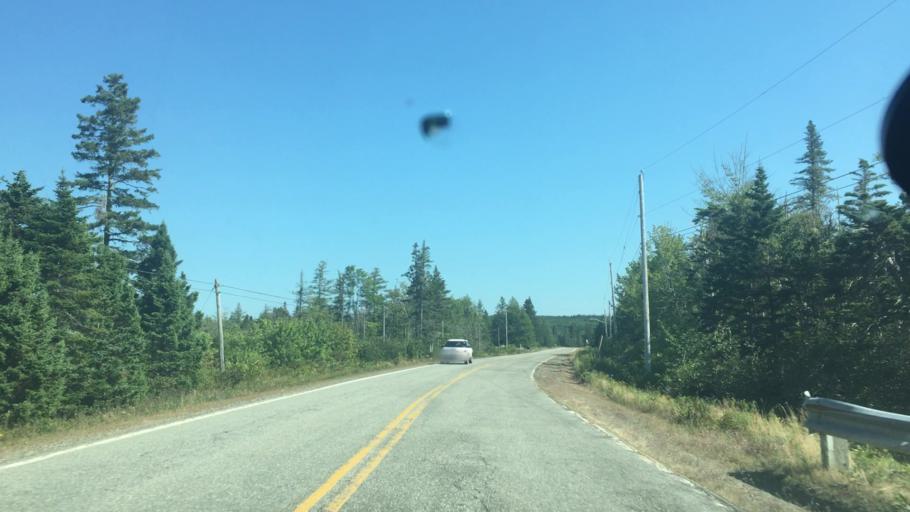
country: CA
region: Nova Scotia
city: New Glasgow
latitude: 44.9009
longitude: -62.4168
